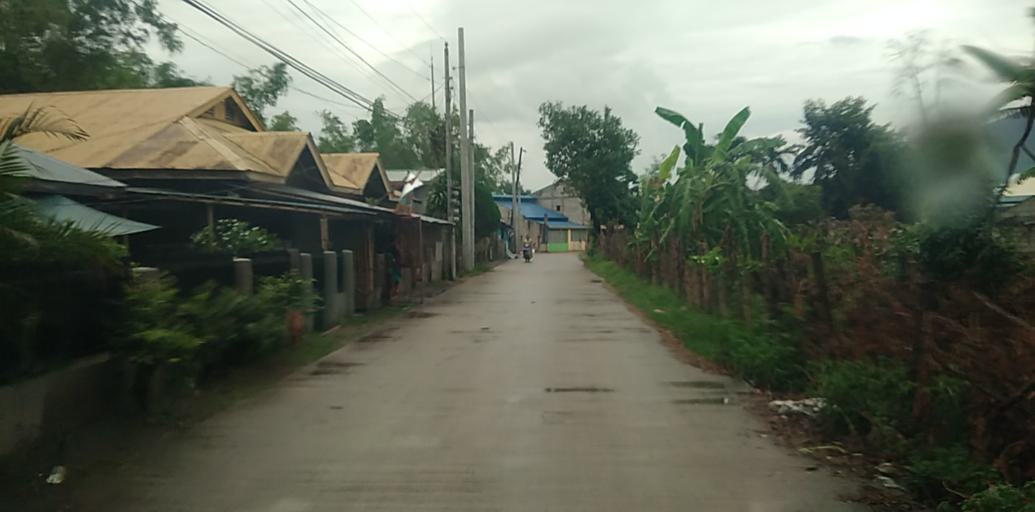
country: PH
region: Central Luzon
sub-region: Province of Pampanga
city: Anao
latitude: 15.1500
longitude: 120.7244
